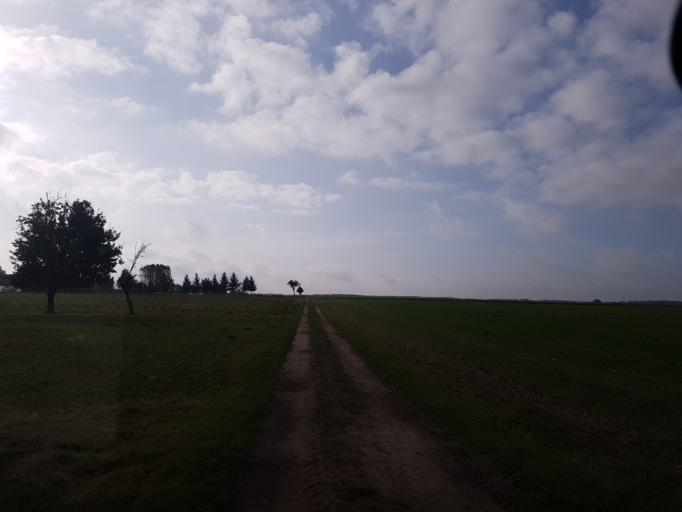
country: DE
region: Brandenburg
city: Finsterwalde
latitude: 51.6294
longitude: 13.7633
